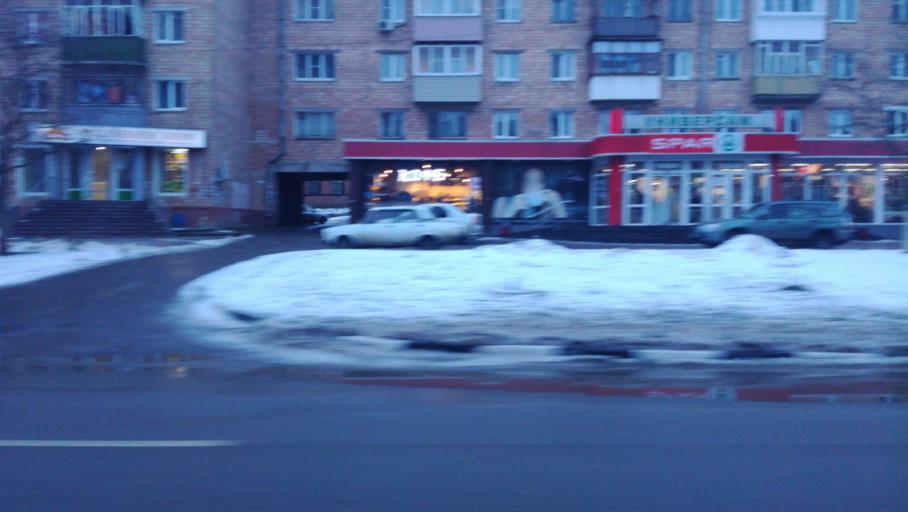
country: RU
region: Tula
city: Tula
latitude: 54.1877
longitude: 37.5923
